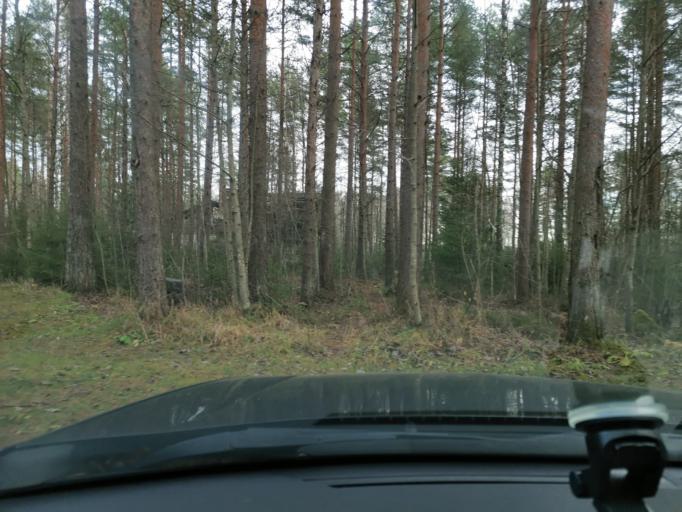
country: EE
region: Ida-Virumaa
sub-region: Sillamaee linn
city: Sillamae
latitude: 59.2543
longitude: 27.9149
